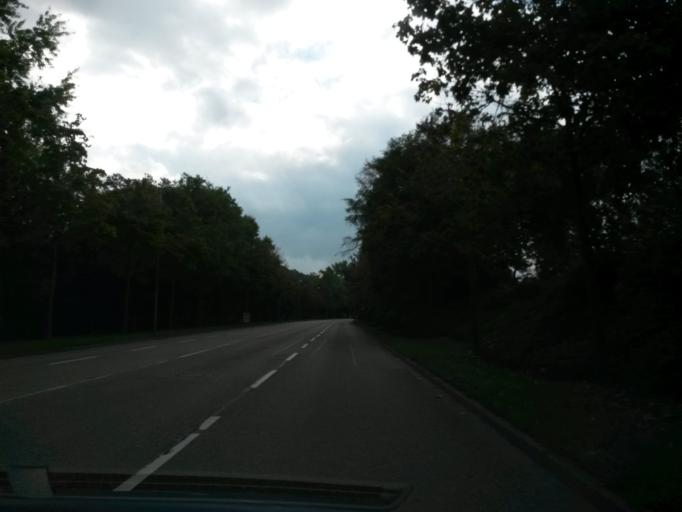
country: DE
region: Baden-Wuerttemberg
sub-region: Karlsruhe Region
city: Pforzheim
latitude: 48.8893
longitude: 8.6771
